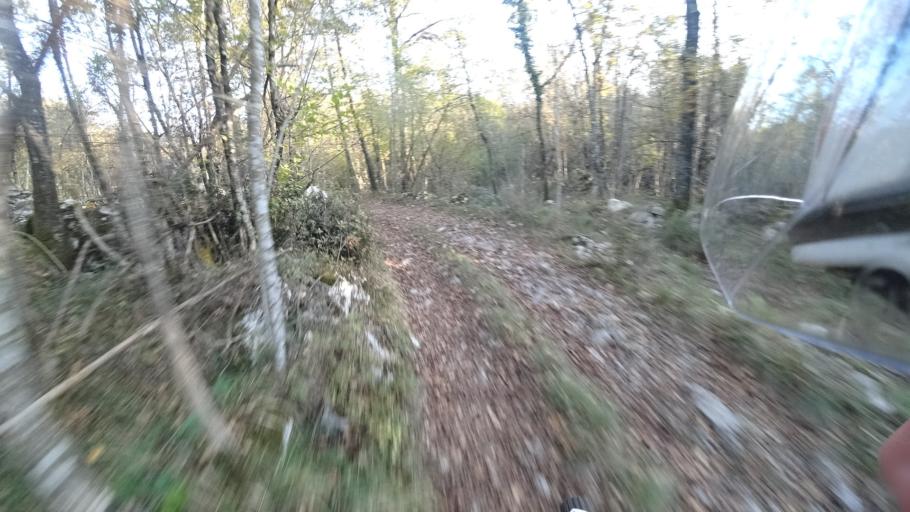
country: HR
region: Primorsko-Goranska
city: Kastav
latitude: 45.4123
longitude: 14.3156
